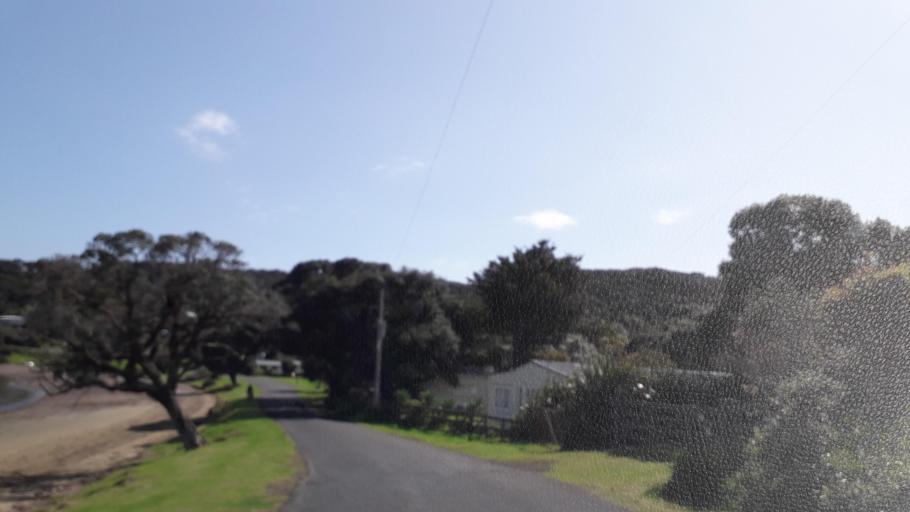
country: NZ
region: Northland
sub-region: Far North District
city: Paihia
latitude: -35.2269
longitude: 174.2637
